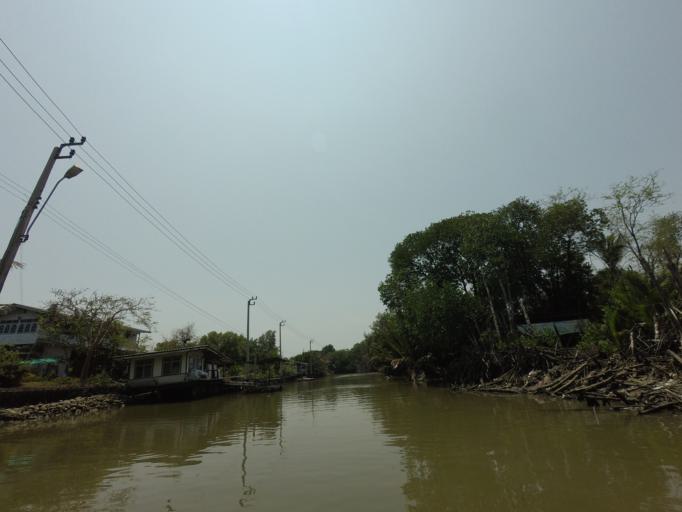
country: TH
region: Bangkok
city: Thung Khru
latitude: 13.5446
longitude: 100.4978
